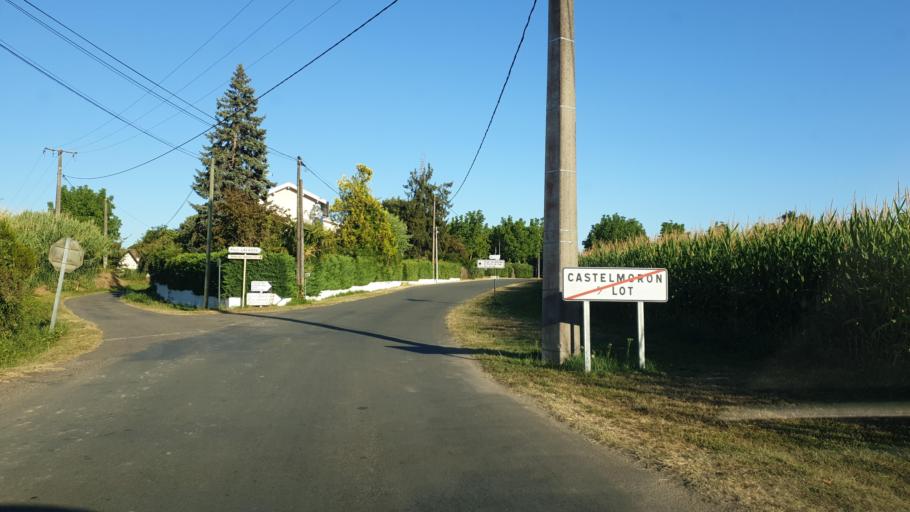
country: FR
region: Aquitaine
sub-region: Departement du Lot-et-Garonne
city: Castelmoron-sur-Lot
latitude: 44.3919
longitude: 0.5040
